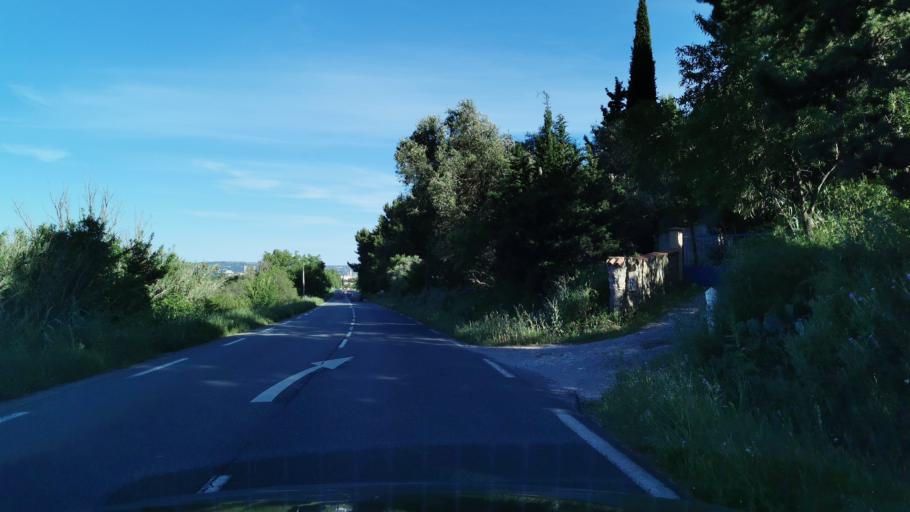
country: FR
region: Languedoc-Roussillon
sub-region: Departement de l'Aude
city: Moussan
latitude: 43.2029
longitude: 2.9652
